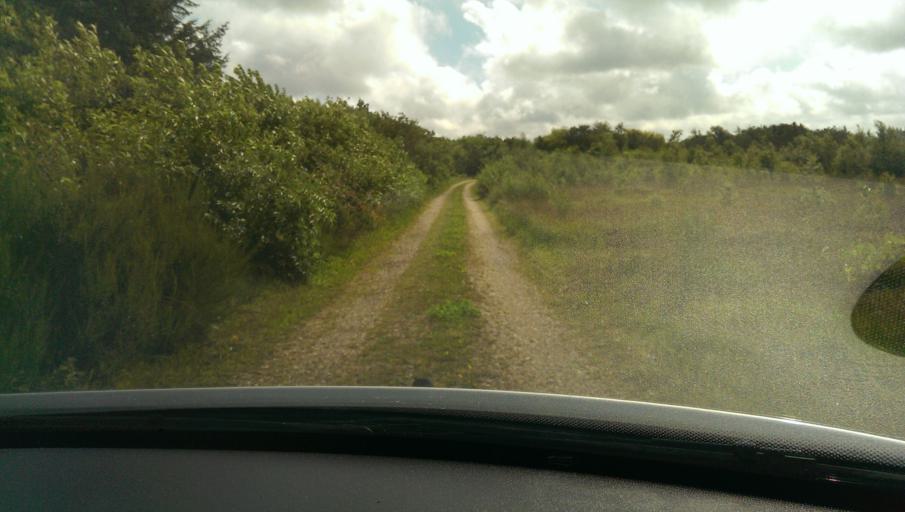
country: DK
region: South Denmark
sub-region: Varde Kommune
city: Varde
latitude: 55.6081
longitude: 8.4443
